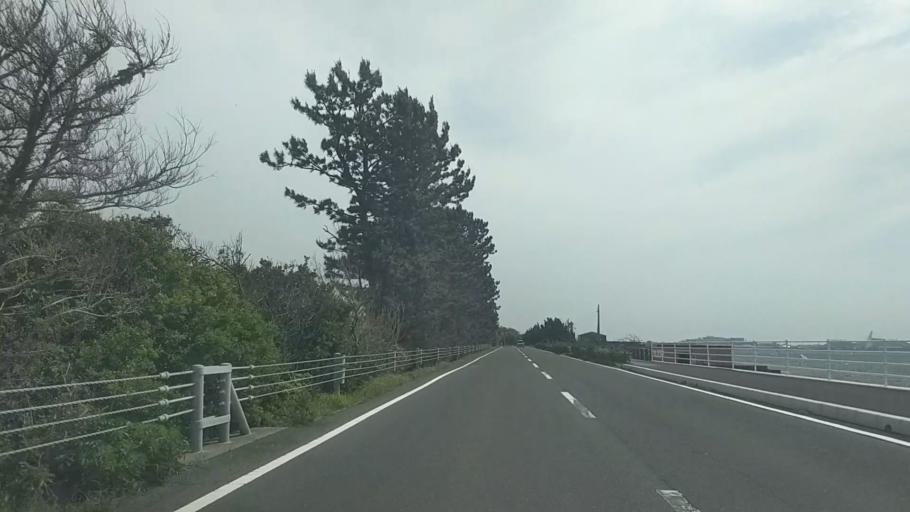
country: JP
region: Shizuoka
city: Kosai-shi
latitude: 34.7160
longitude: 137.5849
